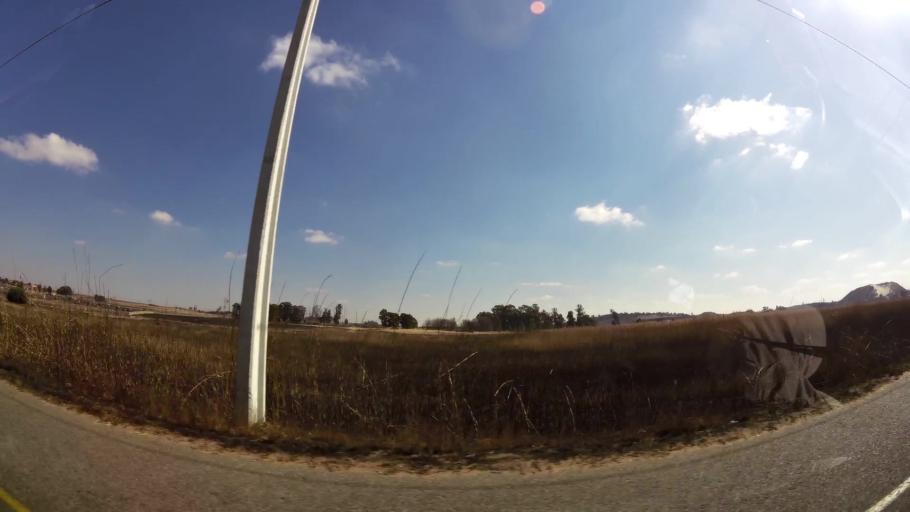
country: ZA
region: Gauteng
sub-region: West Rand District Municipality
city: Krugersdorp
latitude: -26.1507
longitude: 27.7630
